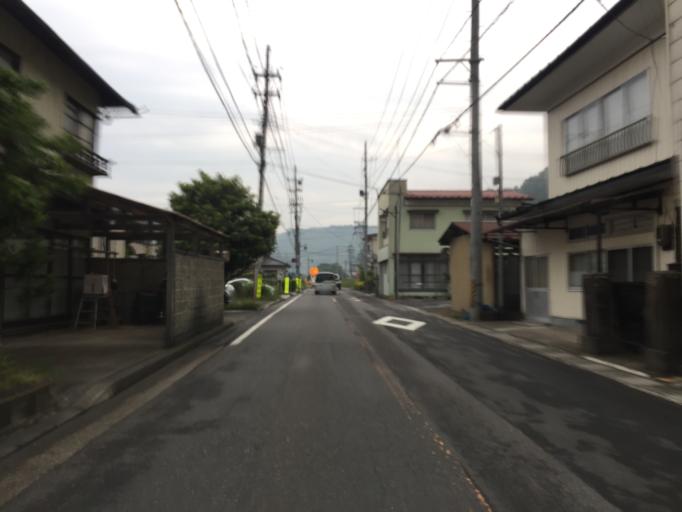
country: JP
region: Fukushima
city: Ishikawa
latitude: 37.1546
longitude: 140.4595
